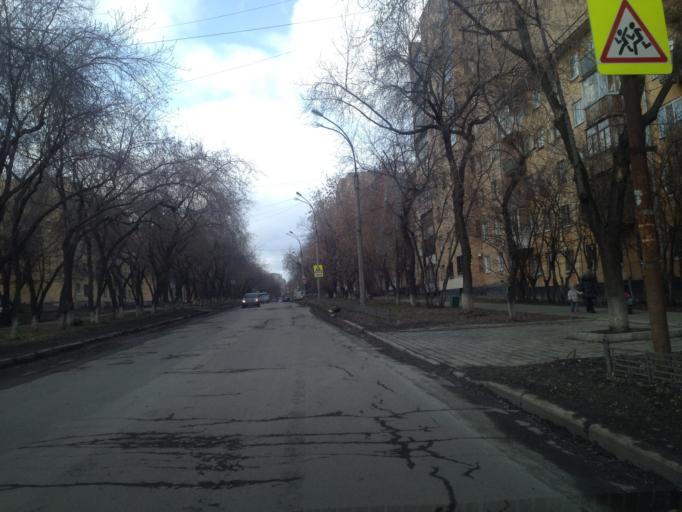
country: RU
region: Sverdlovsk
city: Sovkhoznyy
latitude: 56.7764
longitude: 60.6066
